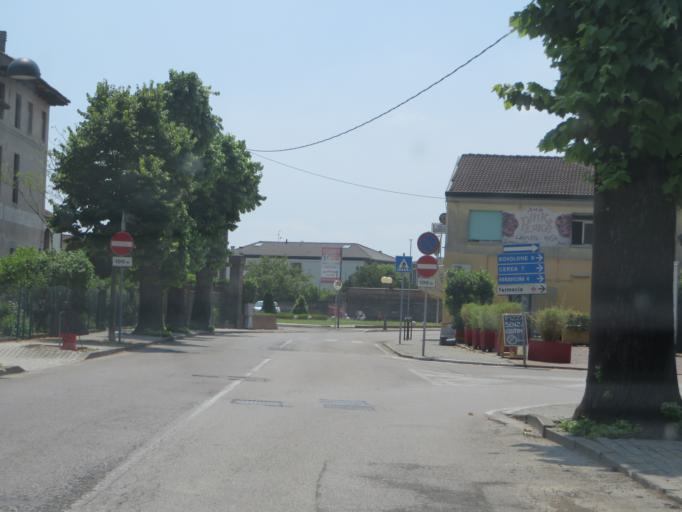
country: IT
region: Veneto
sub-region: Provincia di Verona
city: San Pietro di Morubio
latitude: 45.2474
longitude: 11.2320
